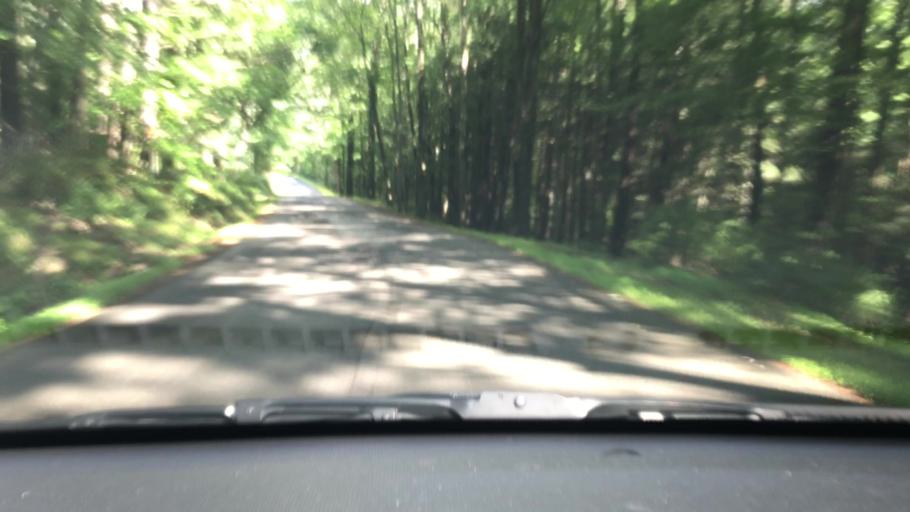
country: US
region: New York
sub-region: Ulster County
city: Shokan
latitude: 41.9635
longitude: -74.2834
